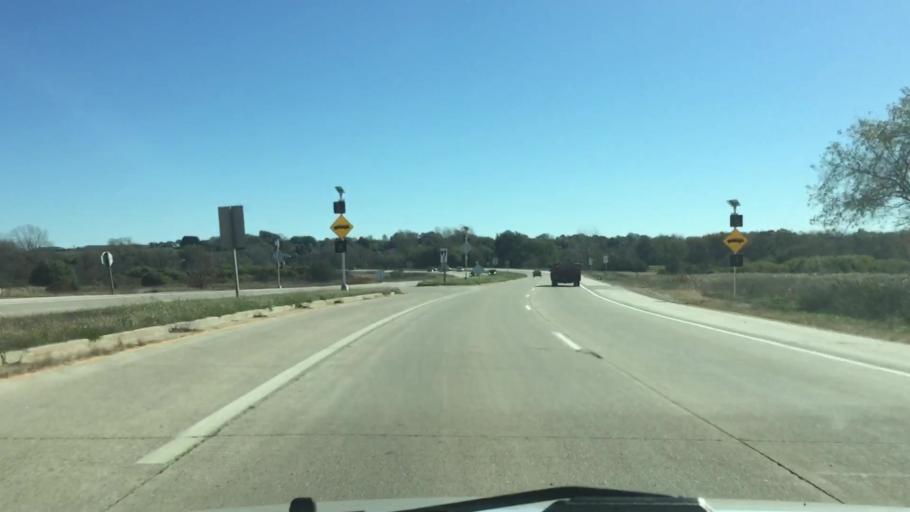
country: US
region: Wisconsin
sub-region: Waukesha County
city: Waukesha
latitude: 42.9791
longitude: -88.2707
